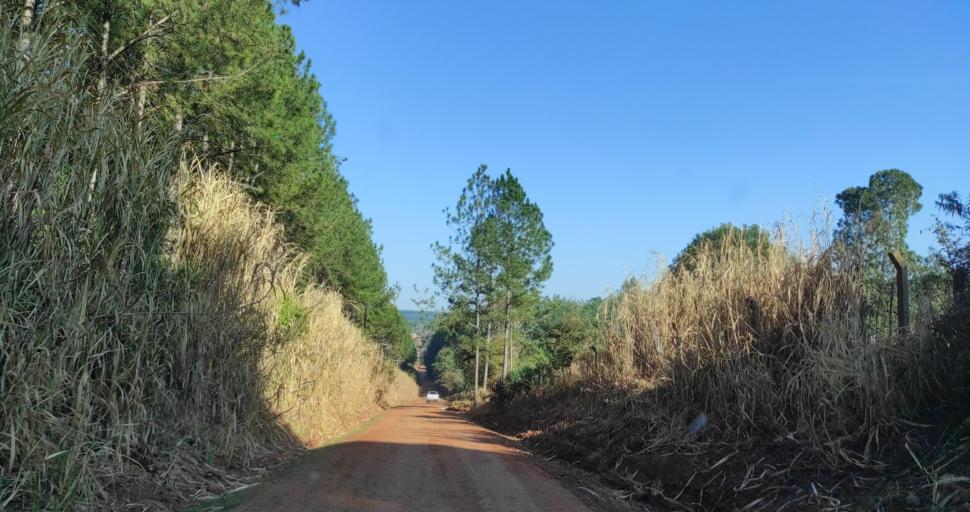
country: AR
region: Misiones
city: Puerto Rico
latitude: -26.8645
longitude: -55.0341
